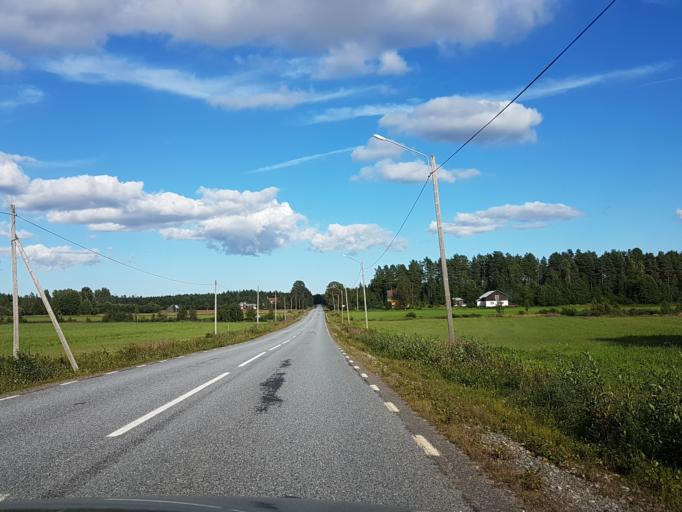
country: SE
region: Vaesterbotten
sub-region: Robertsfors Kommun
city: Robertsfors
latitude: 64.1597
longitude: 20.6545
